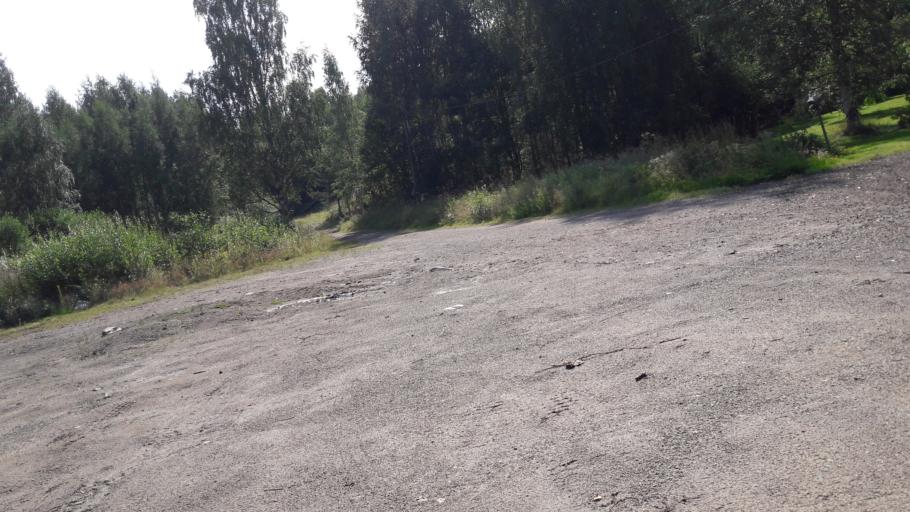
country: FI
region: North Karelia
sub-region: Joensuu
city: Joensuu
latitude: 62.5295
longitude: 29.8514
